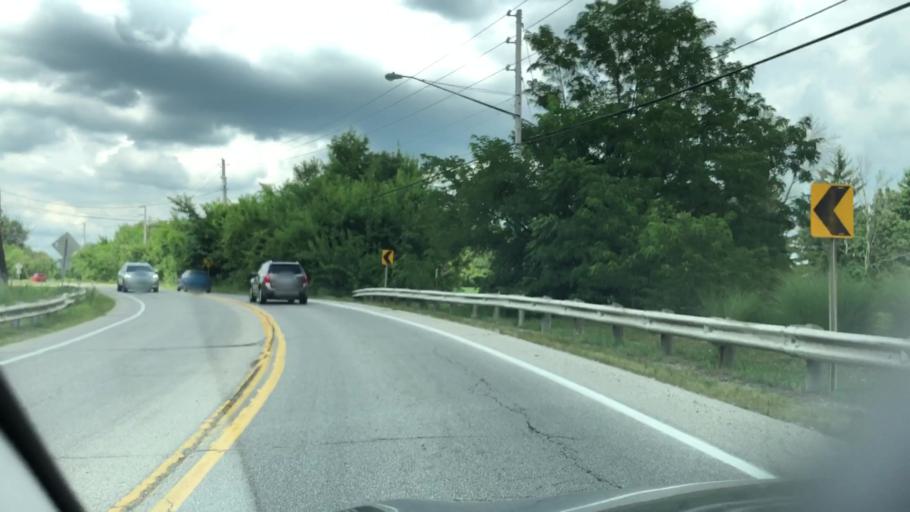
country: US
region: Ohio
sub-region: Summit County
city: Fairlawn
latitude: 41.1281
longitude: -81.6339
